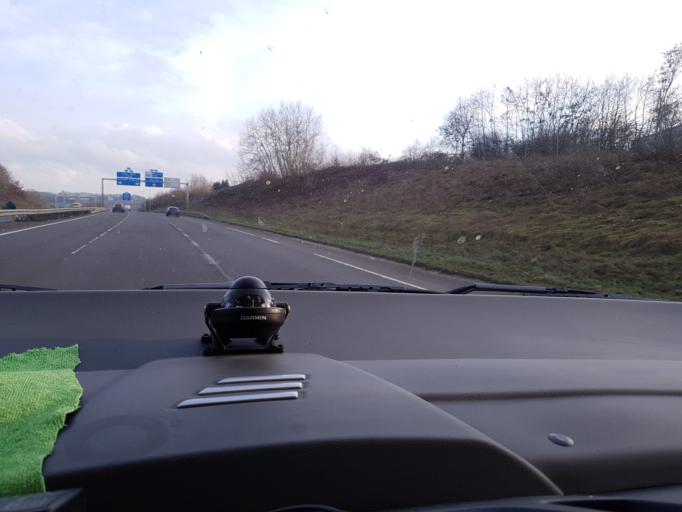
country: FR
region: Champagne-Ardenne
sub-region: Departement des Ardennes
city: La Francheville
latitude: 49.7392
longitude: 4.7115
